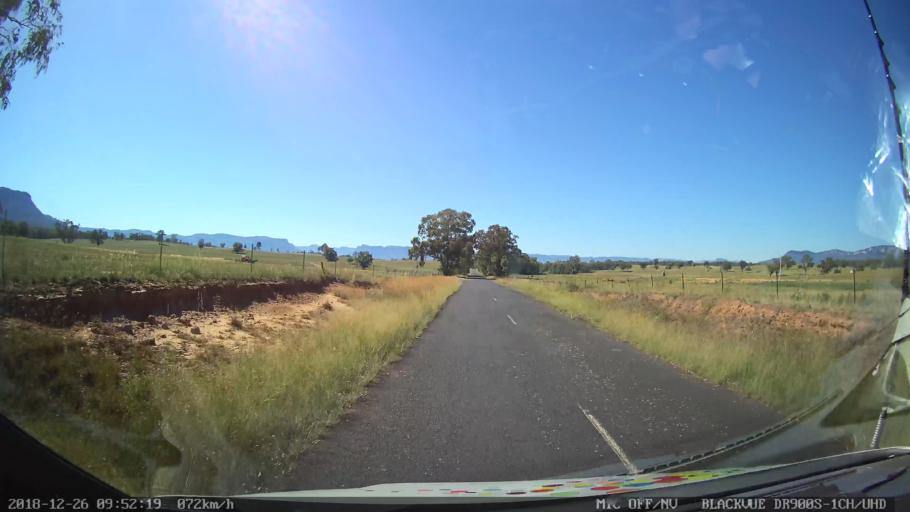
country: AU
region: New South Wales
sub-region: Mid-Western Regional
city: Kandos
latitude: -33.0096
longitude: 150.1483
